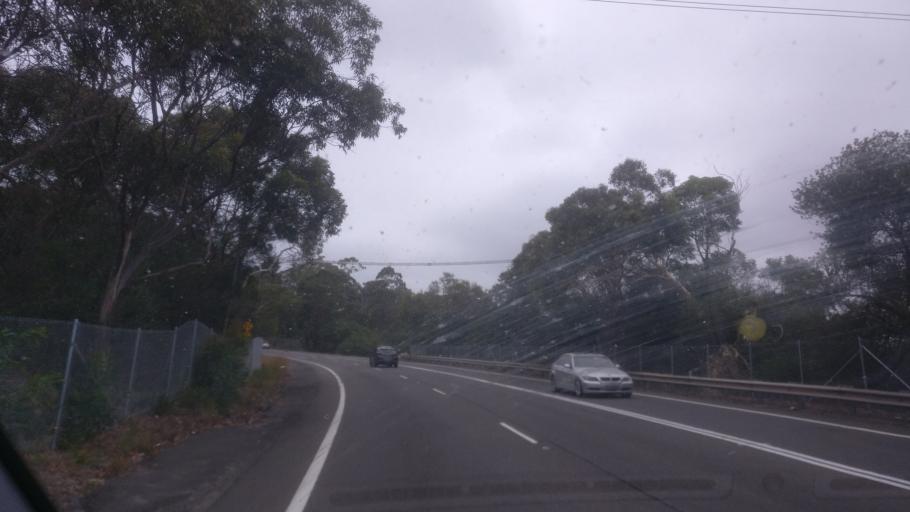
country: AU
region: New South Wales
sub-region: Warringah
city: Allambie Heights
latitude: -33.7447
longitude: 151.2355
